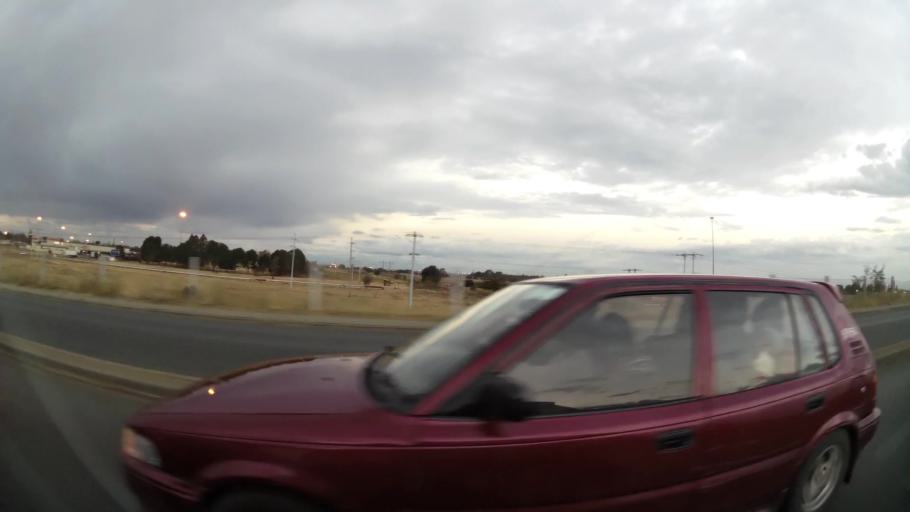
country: ZA
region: Orange Free State
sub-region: Lejweleputswa District Municipality
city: Welkom
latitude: -27.9764
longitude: 26.7744
